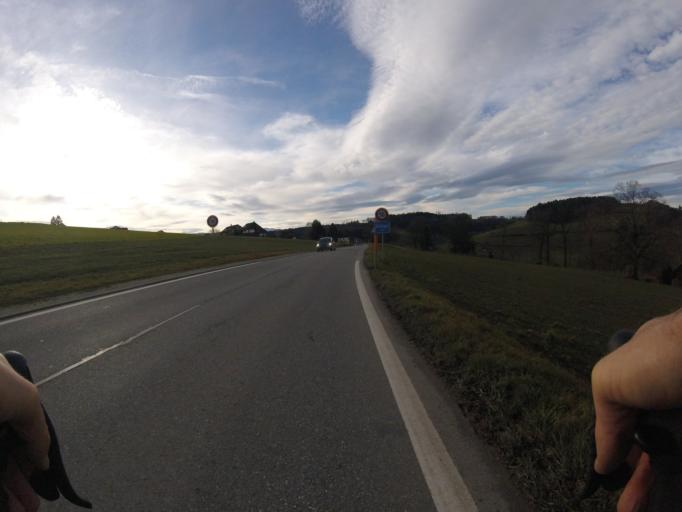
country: CH
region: Fribourg
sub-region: Sense District
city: Ueberstorf
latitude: 46.8557
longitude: 7.3162
